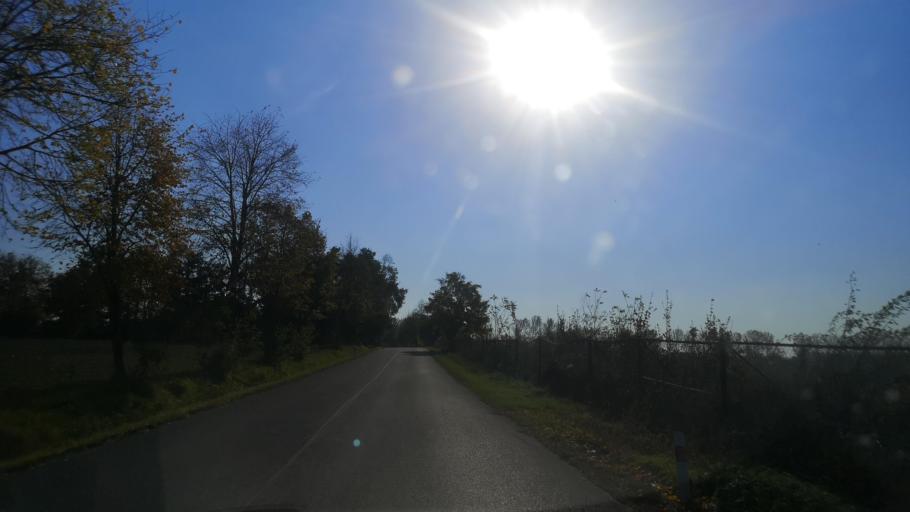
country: SK
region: Nitriansky
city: Zlate Moravce
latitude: 48.4269
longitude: 18.4247
